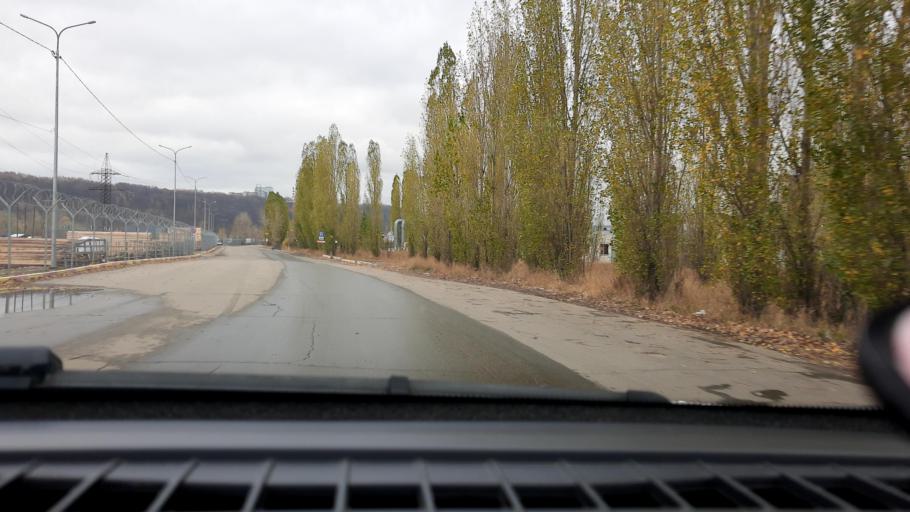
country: RU
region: Nizjnij Novgorod
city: Nizhniy Novgorod
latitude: 56.2545
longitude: 43.9365
